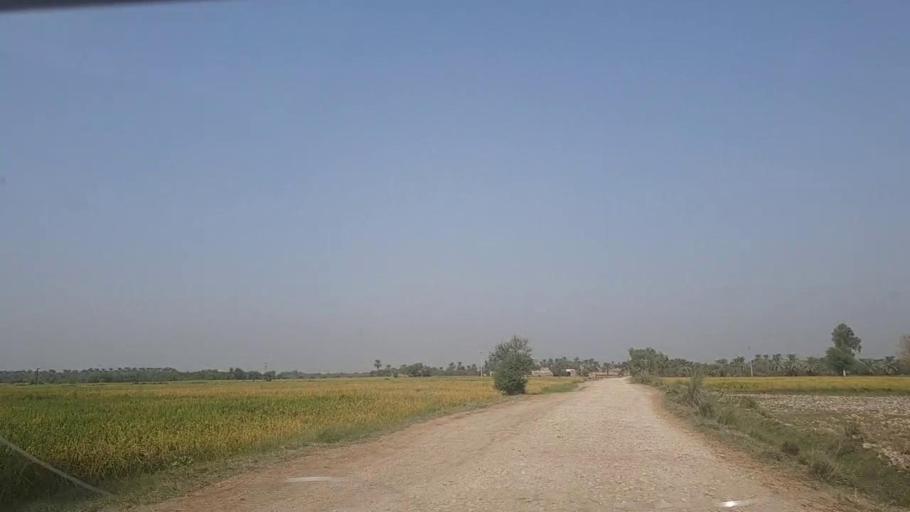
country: PK
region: Sindh
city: Madeji
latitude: 27.8029
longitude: 68.4257
